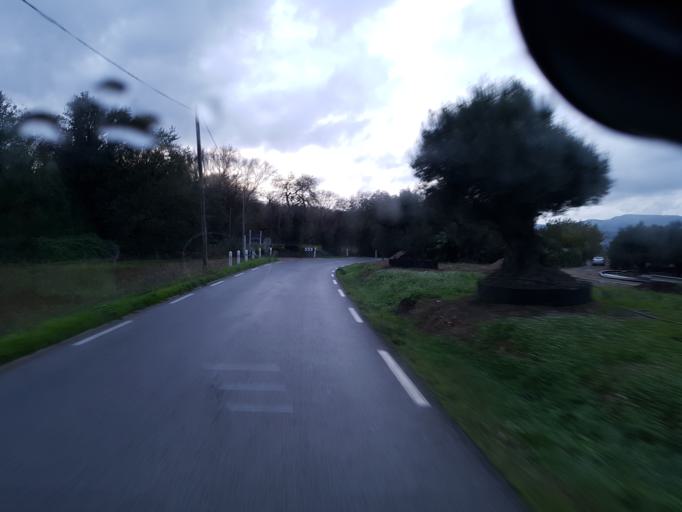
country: FR
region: Provence-Alpes-Cote d'Azur
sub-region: Departement du Var
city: Cogolin
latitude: 43.2651
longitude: 6.5615
